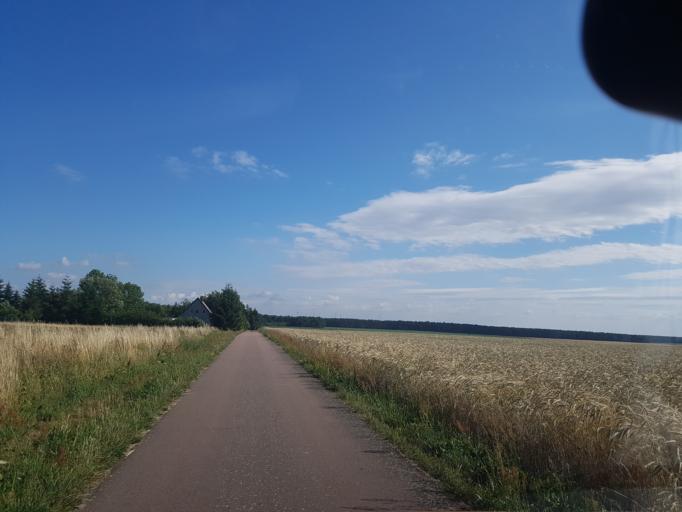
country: DE
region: Brandenburg
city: Juterbog
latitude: 51.9027
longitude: 13.1381
